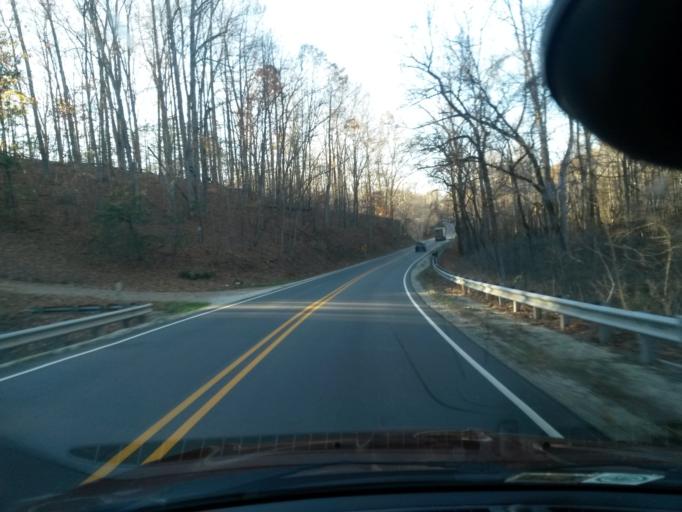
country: US
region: Virginia
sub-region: Amherst County
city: Amherst
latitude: 37.6199
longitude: -79.1036
